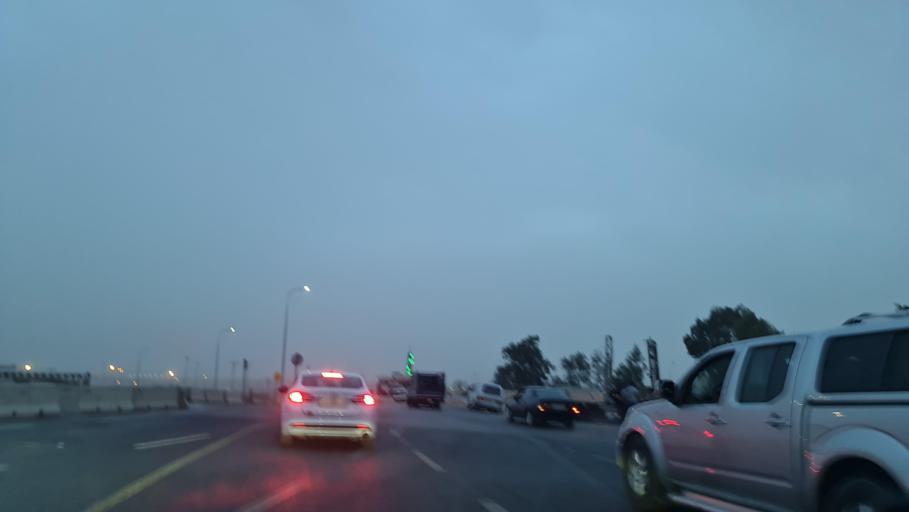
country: JO
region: Zarqa
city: Russeifa
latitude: 32.0160
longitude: 36.0704
